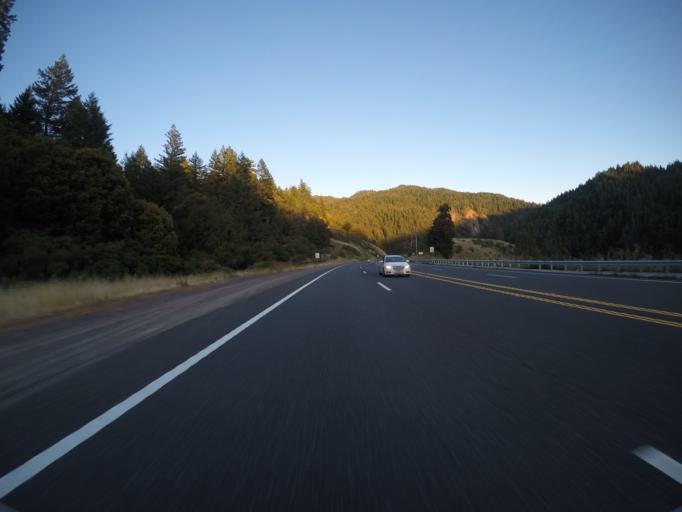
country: US
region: California
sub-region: Humboldt County
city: Redway
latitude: 39.9321
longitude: -123.7653
